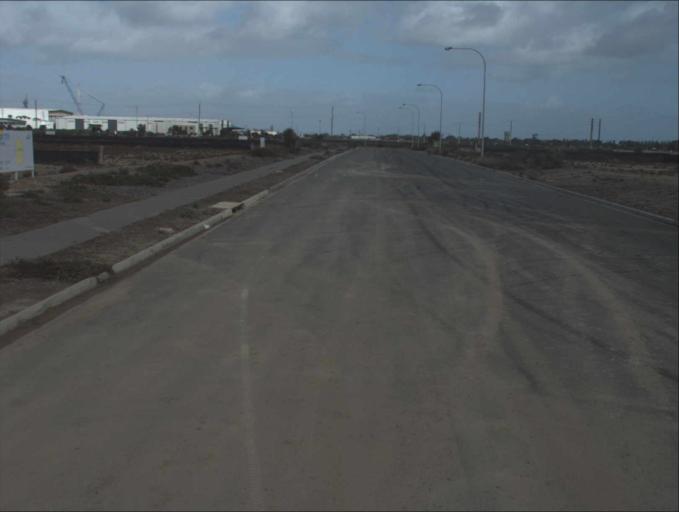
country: AU
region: South Australia
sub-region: Port Adelaide Enfield
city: Birkenhead
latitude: -34.7742
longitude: 138.5064
